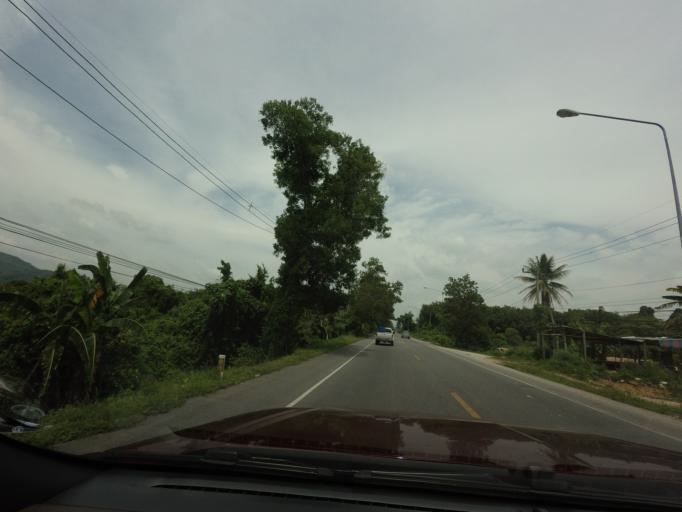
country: TH
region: Yala
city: Yala
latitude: 6.6006
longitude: 101.3022
